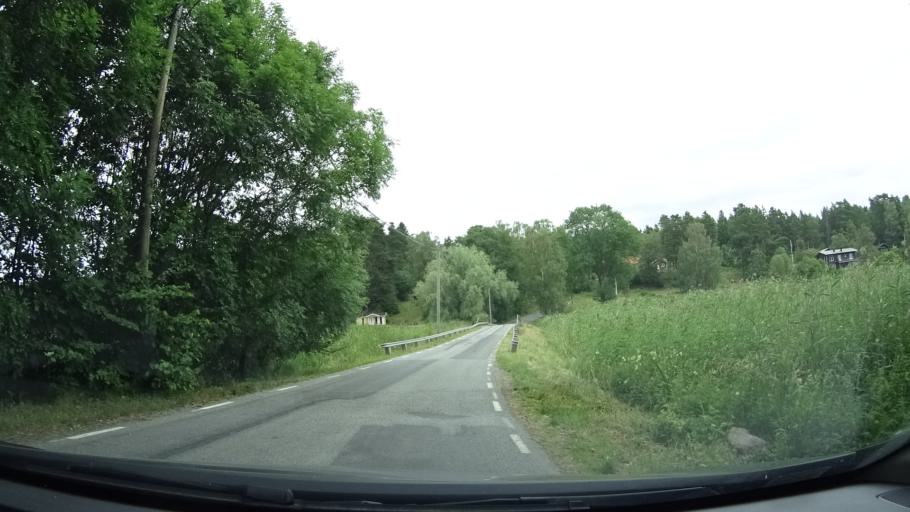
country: SE
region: Stockholm
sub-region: Varmdo Kommun
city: Mortnas
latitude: 59.3706
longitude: 18.4656
